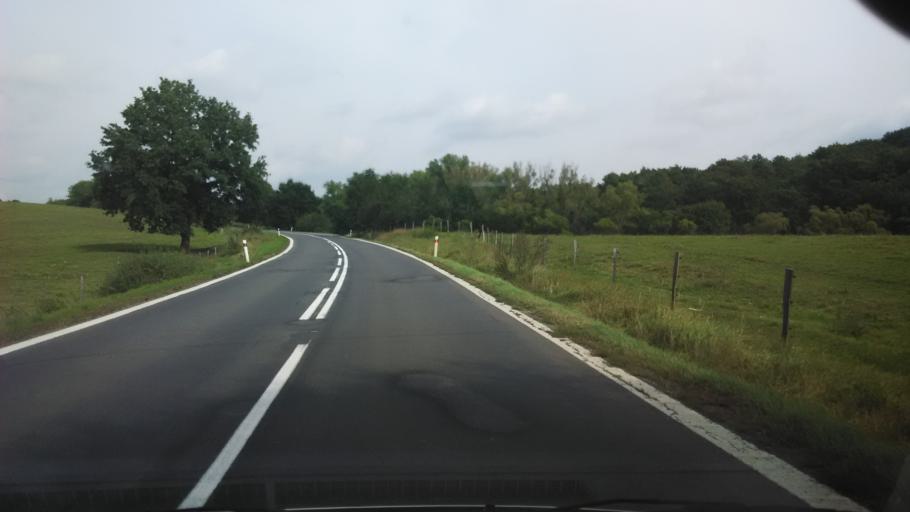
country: SK
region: Banskobystricky
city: Krupina
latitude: 48.2926
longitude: 19.0186
